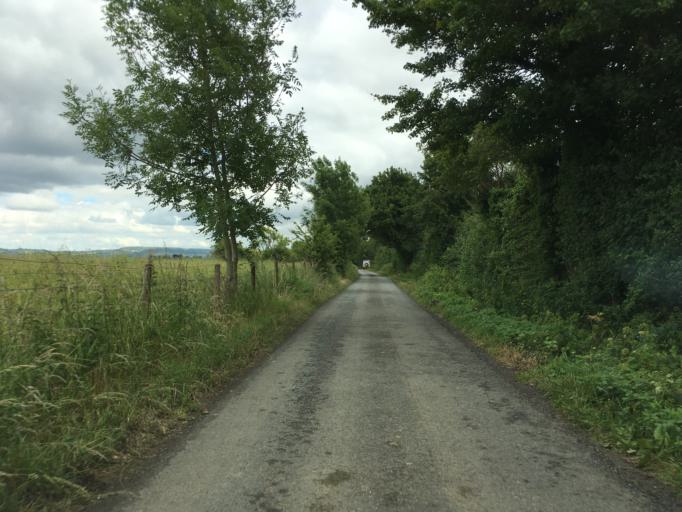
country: GB
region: England
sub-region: Gloucestershire
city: Stonehouse
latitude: 51.7942
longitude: -2.3800
